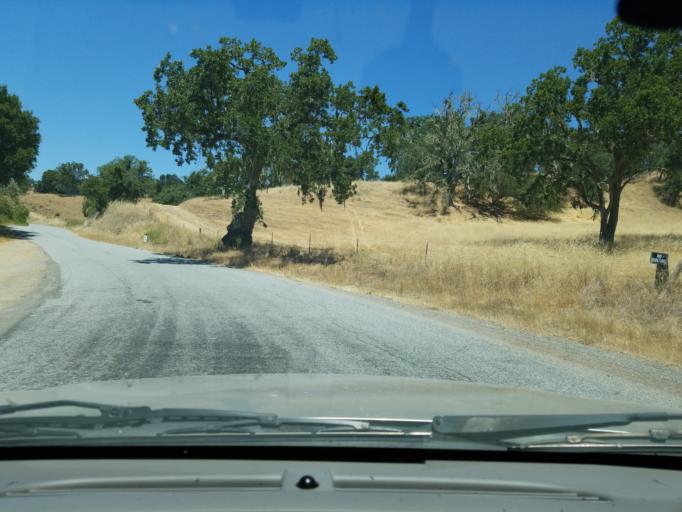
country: US
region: California
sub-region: Monterey County
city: Gonzales
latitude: 36.3995
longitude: -121.5766
